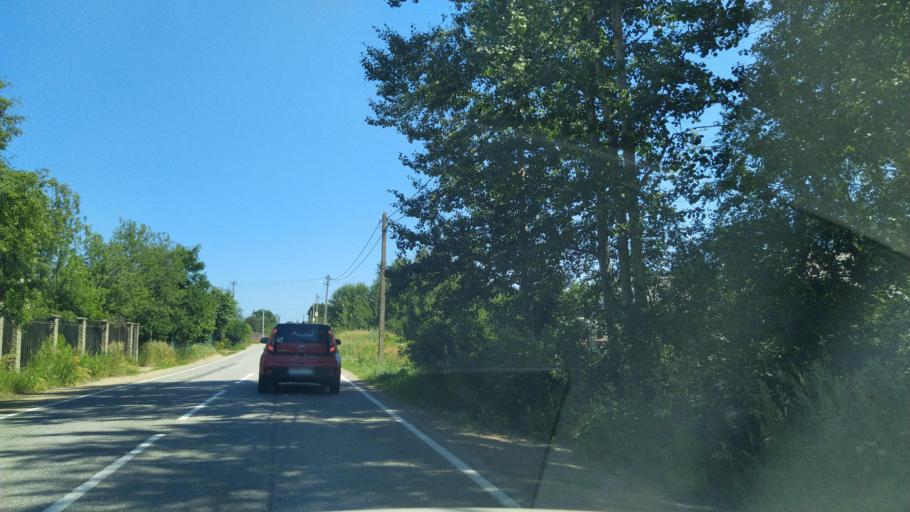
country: RU
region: Leningrad
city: Borisova Griva
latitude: 60.0839
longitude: 31.0218
